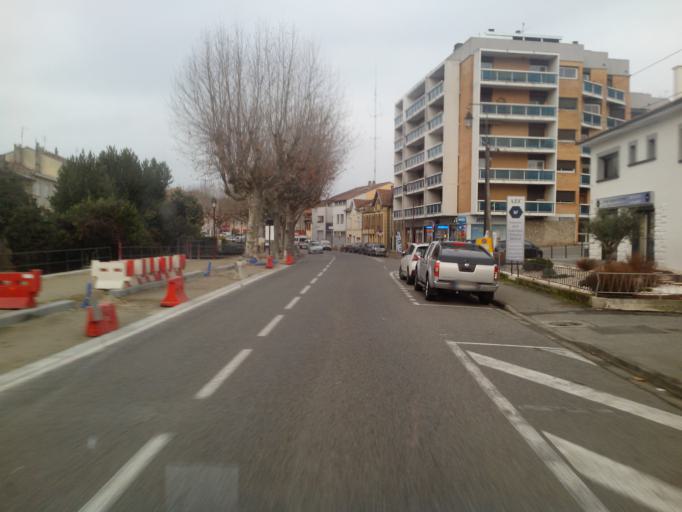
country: FR
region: Midi-Pyrenees
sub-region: Departement de l'Ariege
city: Pamiers
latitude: 43.1142
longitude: 1.6133
